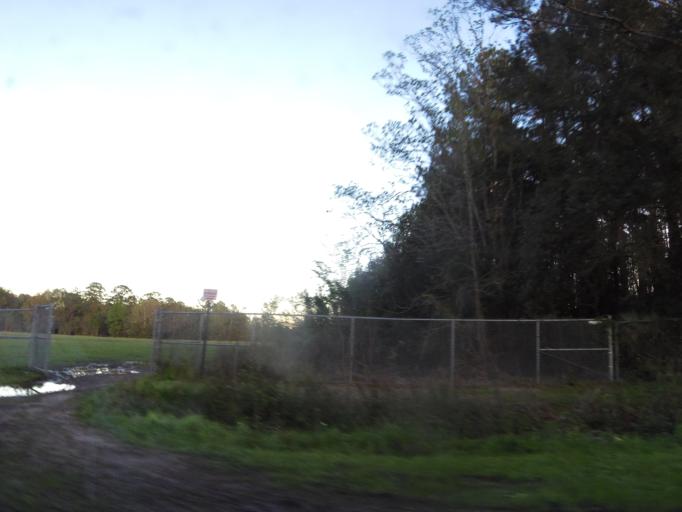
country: US
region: Florida
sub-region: Duval County
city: Jacksonville
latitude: 30.3468
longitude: -81.7292
